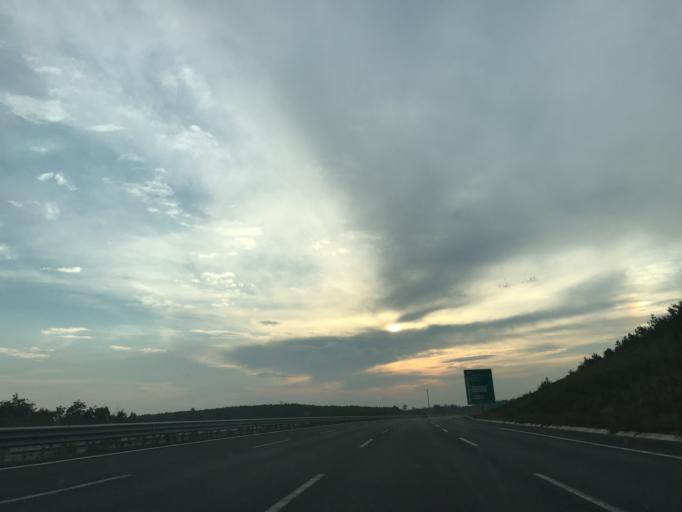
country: TR
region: Istanbul
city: Sancaktepe
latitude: 41.0431
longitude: 29.2152
